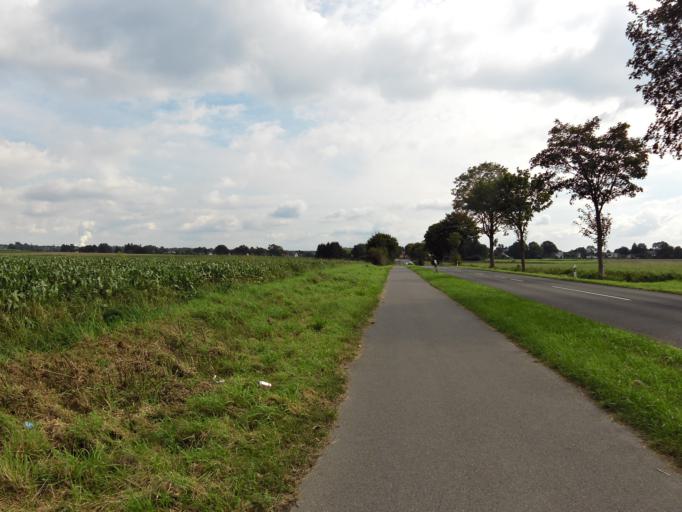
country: NL
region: Limburg
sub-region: Gemeente Kerkrade
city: Kerkrade
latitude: 50.8385
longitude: 6.0355
